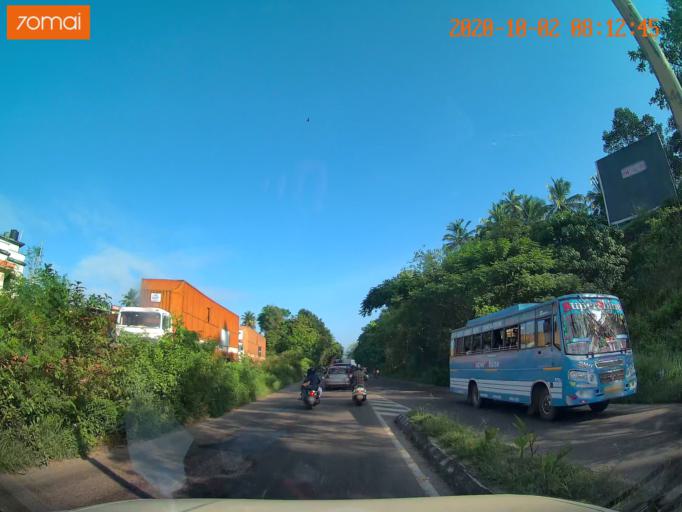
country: IN
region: Kerala
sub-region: Kozhikode
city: Kozhikode
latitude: 11.2837
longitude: 75.8025
